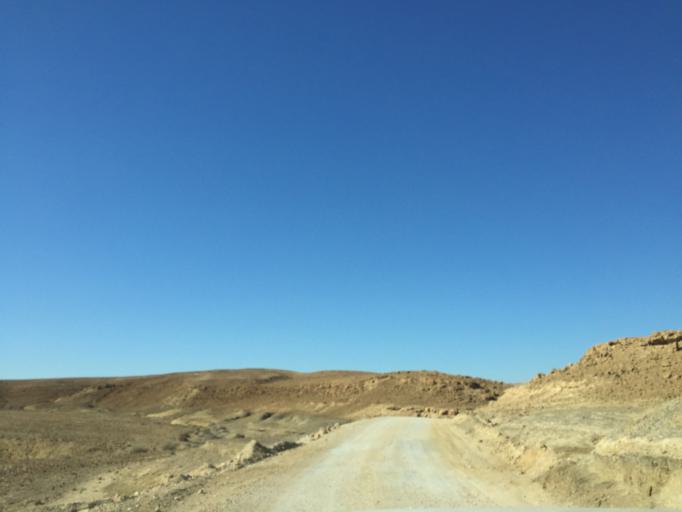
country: IL
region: Southern District
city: Mitzpe Ramon
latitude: 30.6122
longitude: 34.9338
